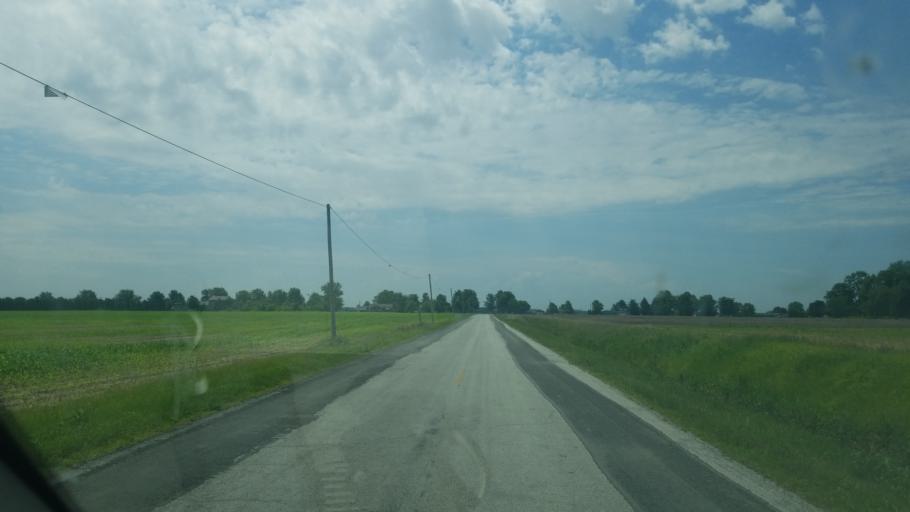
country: US
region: Ohio
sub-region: Wood County
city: North Baltimore
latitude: 41.2581
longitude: -83.5930
